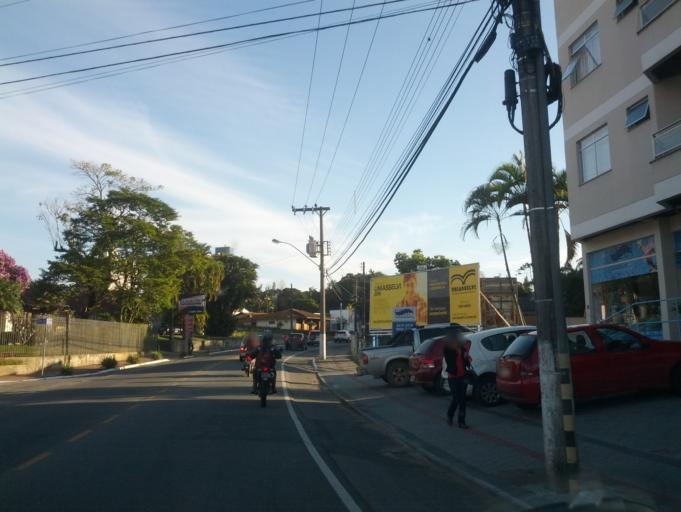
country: BR
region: Santa Catarina
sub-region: Indaial
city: Indaial
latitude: -26.8934
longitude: -49.2271
